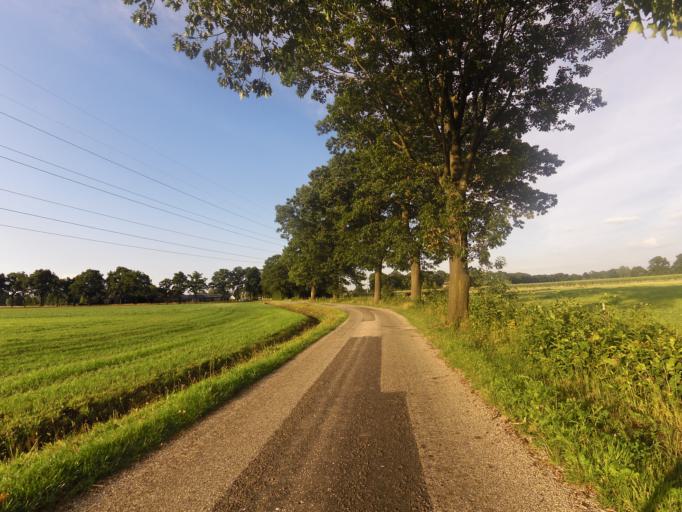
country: NL
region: Gelderland
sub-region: Oude IJsselstreek
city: Varsseveld
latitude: 51.9139
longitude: 6.4760
